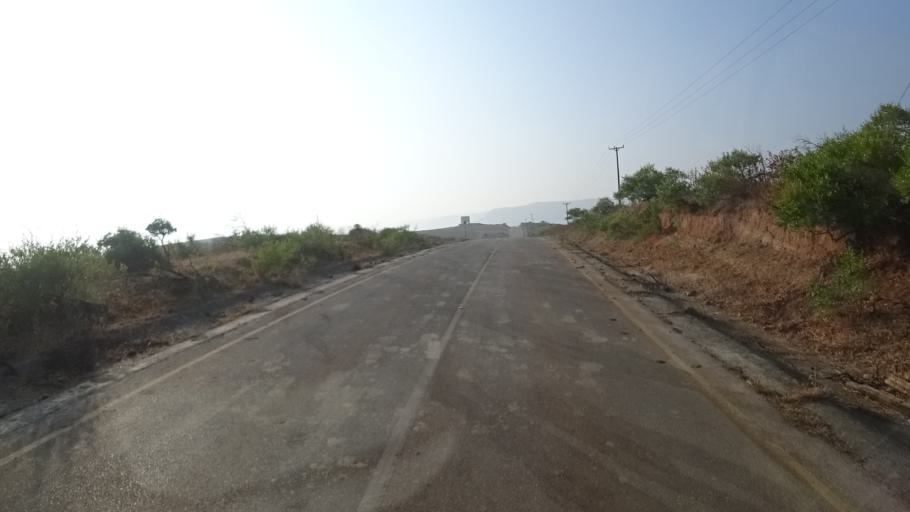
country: YE
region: Al Mahrah
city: Hawf
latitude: 16.7447
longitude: 53.3507
